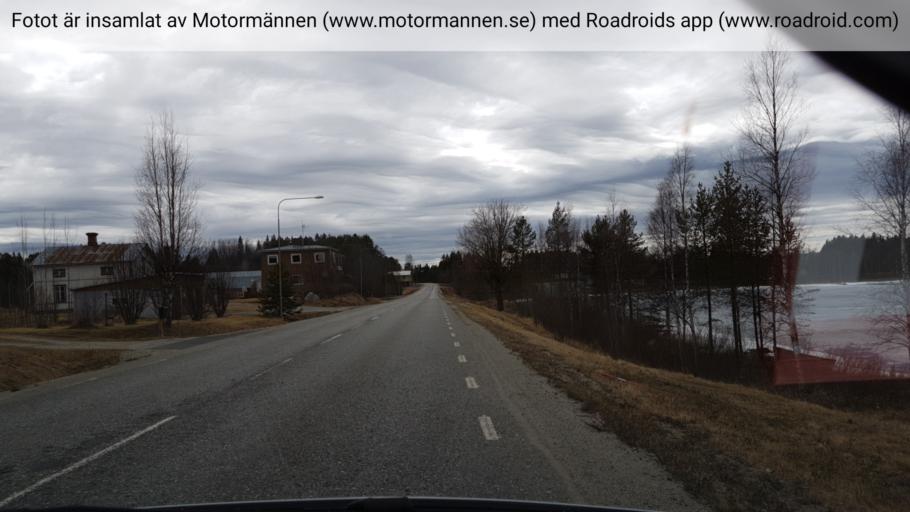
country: SE
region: Vaesterbotten
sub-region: Asele Kommun
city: Asele
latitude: 63.9377
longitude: 17.2791
